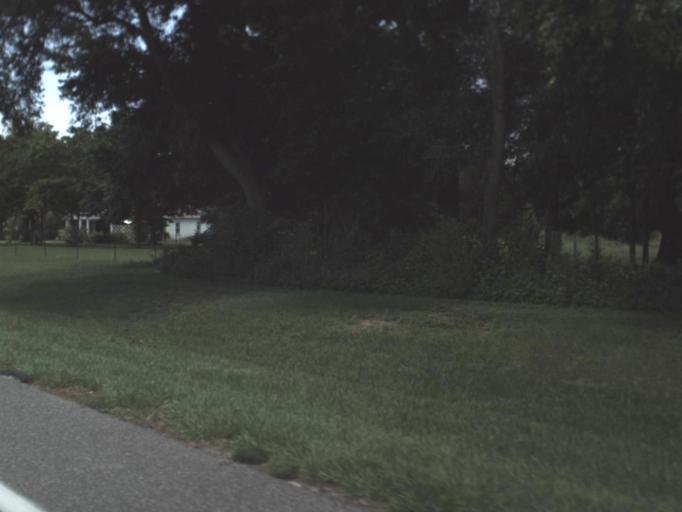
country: US
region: Florida
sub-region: Lafayette County
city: Mayo
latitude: 30.0425
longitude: -83.0754
